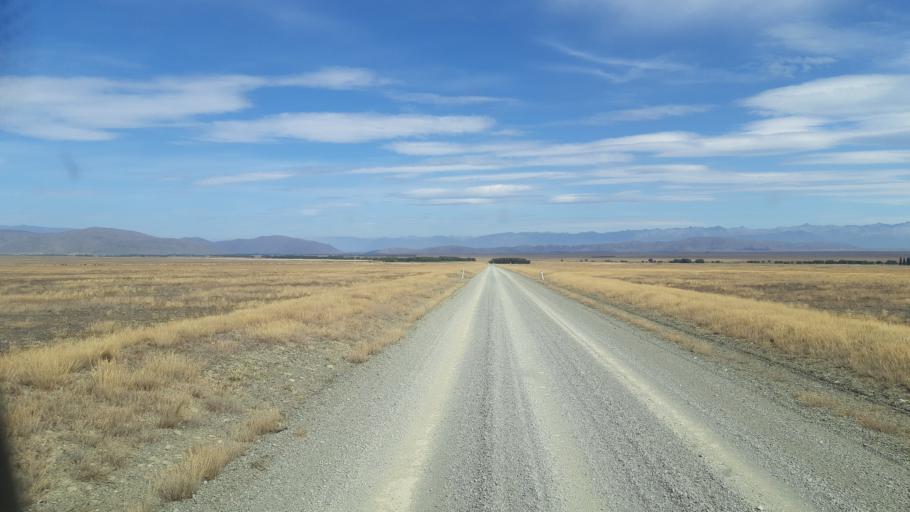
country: NZ
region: Canterbury
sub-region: Timaru District
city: Pleasant Point
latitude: -44.1949
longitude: 170.5369
